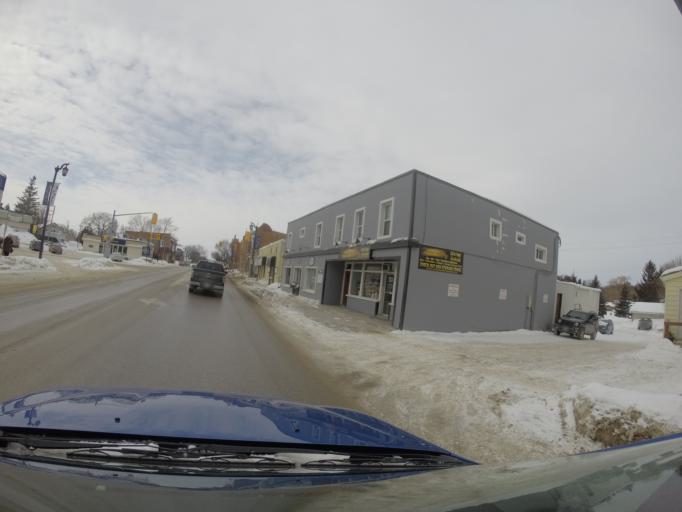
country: CA
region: Ontario
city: Wasaga Beach
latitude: 44.4197
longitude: -80.0900
